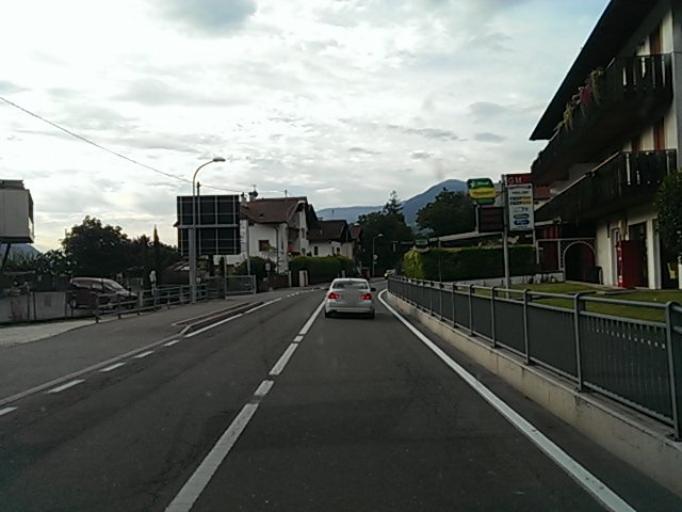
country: IT
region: Trentino-Alto Adige
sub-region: Bolzano
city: Marlengo
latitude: 46.6529
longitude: 11.1468
